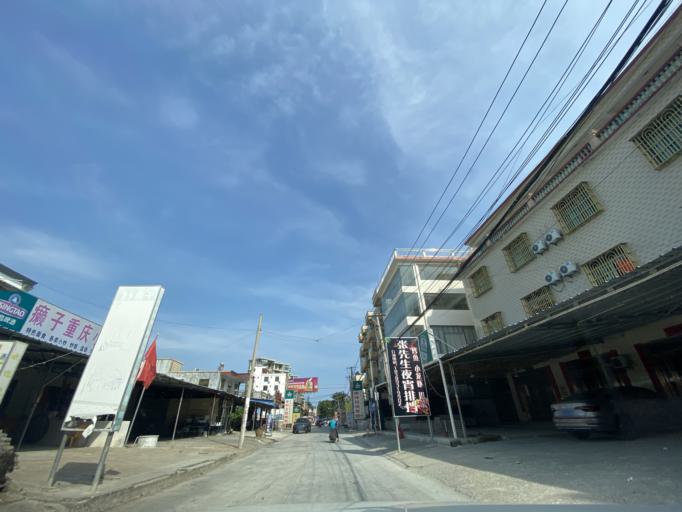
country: CN
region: Hainan
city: Yingzhou
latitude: 18.4036
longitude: 109.8434
